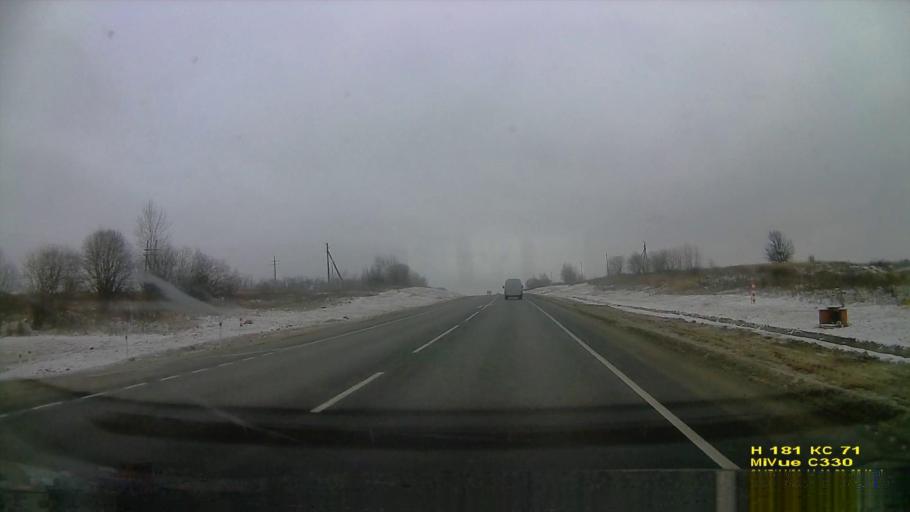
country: RU
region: Tula
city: Leninskiy
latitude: 54.2152
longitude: 37.3950
